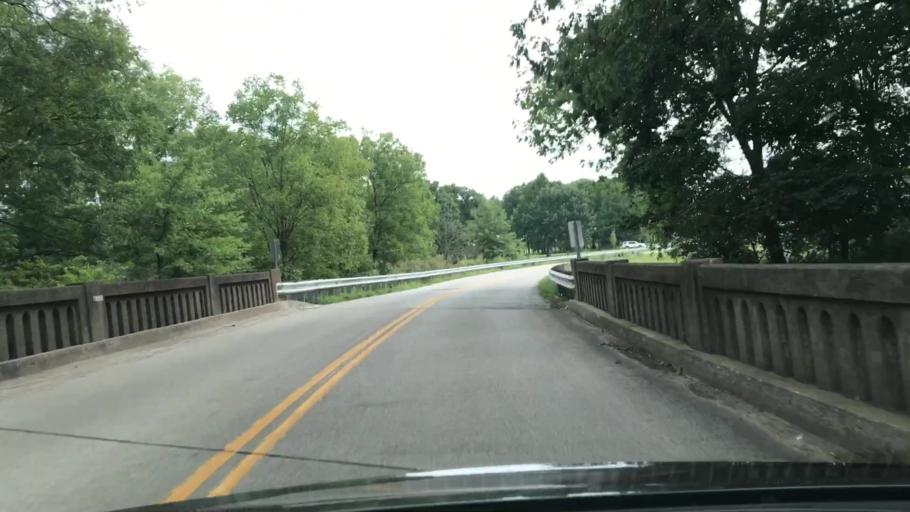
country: US
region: Kentucky
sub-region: Todd County
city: Elkton
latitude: 36.7920
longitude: -87.1391
